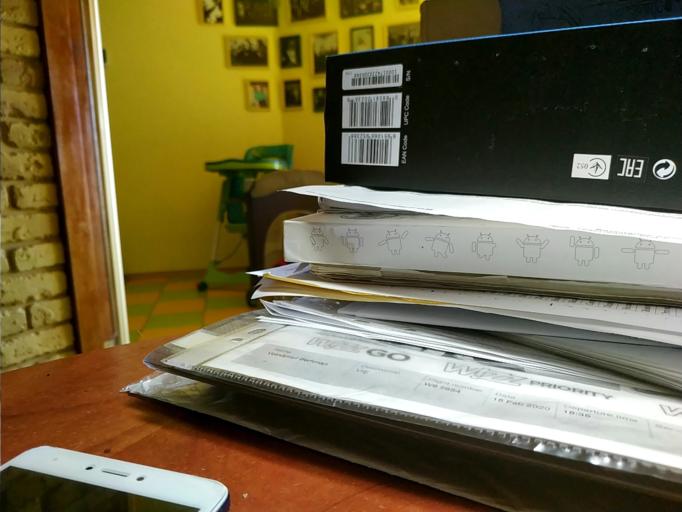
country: RU
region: Novgorod
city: Kholm
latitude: 59.2515
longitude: 32.8475
